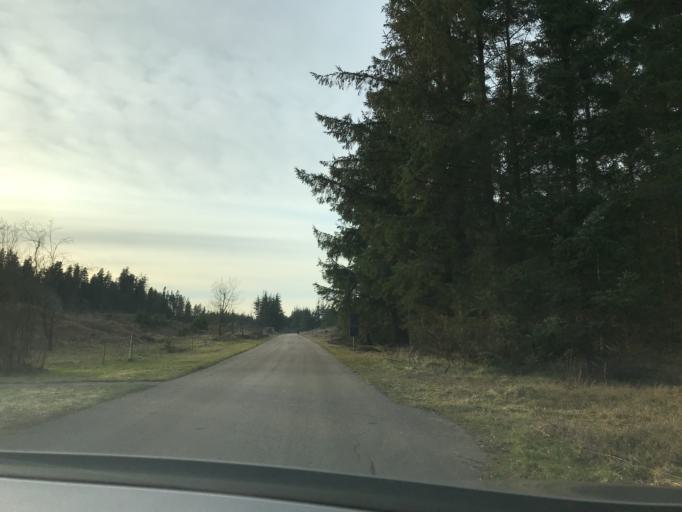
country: DK
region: South Denmark
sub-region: Varde Kommune
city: Oksbol
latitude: 55.7941
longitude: 8.2228
